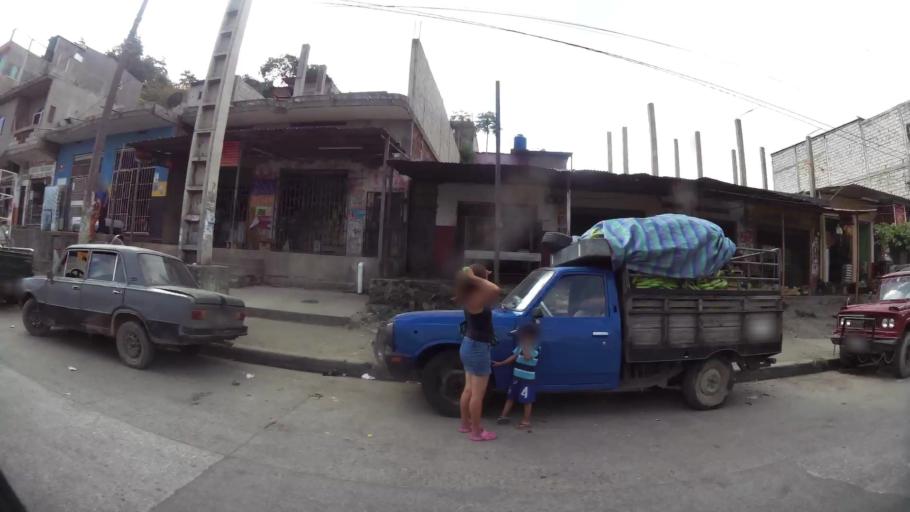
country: EC
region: Guayas
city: Santa Lucia
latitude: -2.1200
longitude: -79.9691
